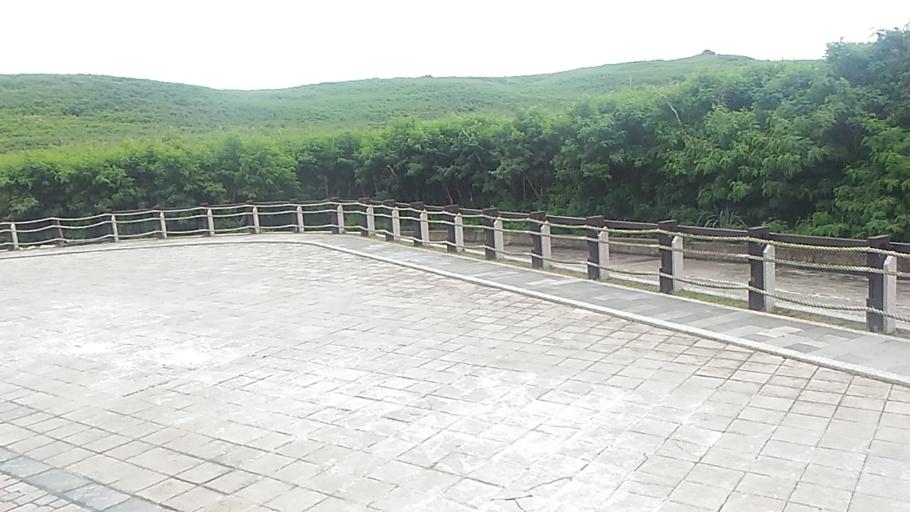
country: TW
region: Taiwan
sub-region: Penghu
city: Ma-kung
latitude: 23.3740
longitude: 119.4973
